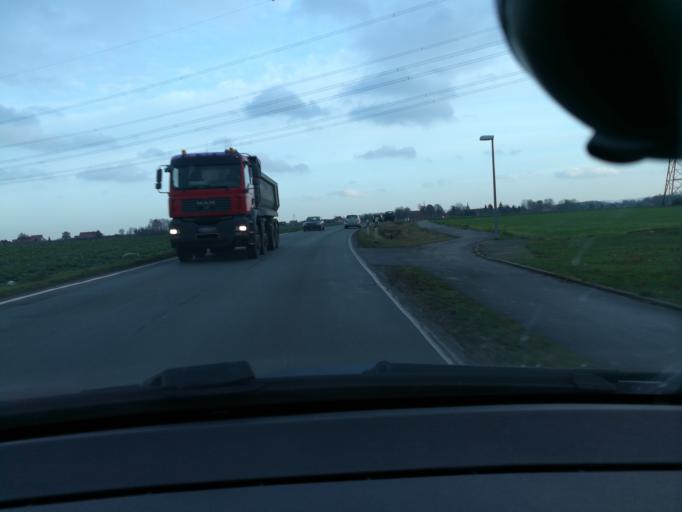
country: DE
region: North Rhine-Westphalia
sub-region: Regierungsbezirk Detmold
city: Hille
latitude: 52.3182
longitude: 8.8041
